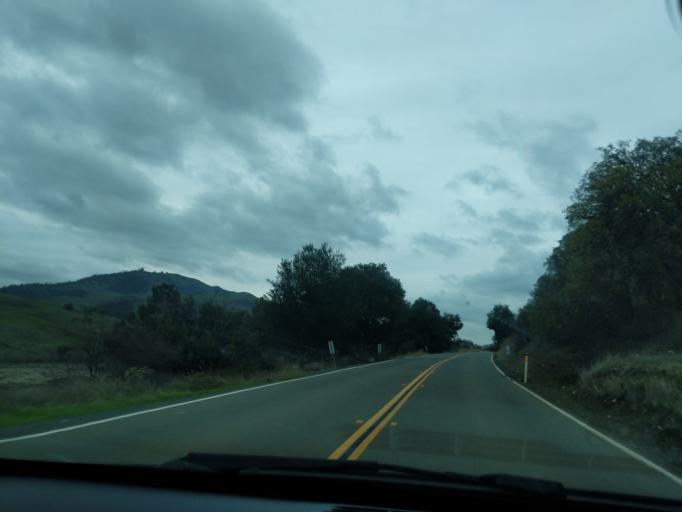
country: US
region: California
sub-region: Monterey County
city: Soledad
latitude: 36.6048
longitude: -121.1977
